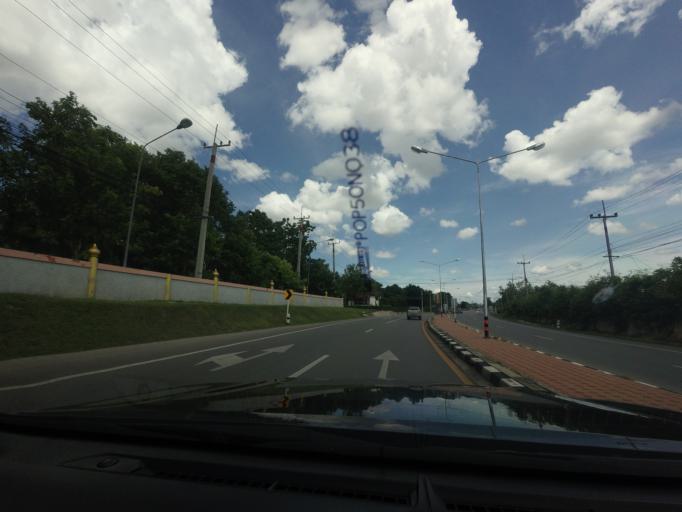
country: TH
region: Kanchanaburi
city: Kanchanaburi
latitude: 14.0796
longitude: 99.4746
